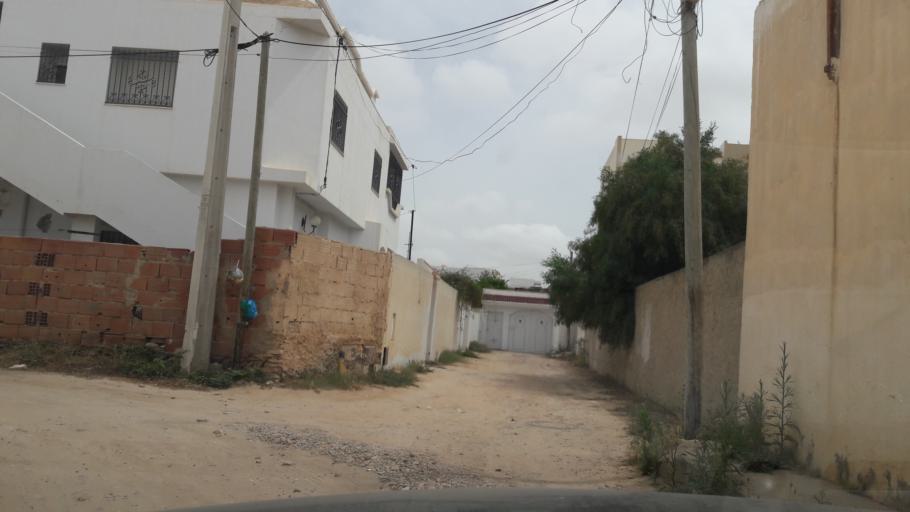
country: TN
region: Safaqis
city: Sfax
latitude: 34.7724
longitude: 10.7589
